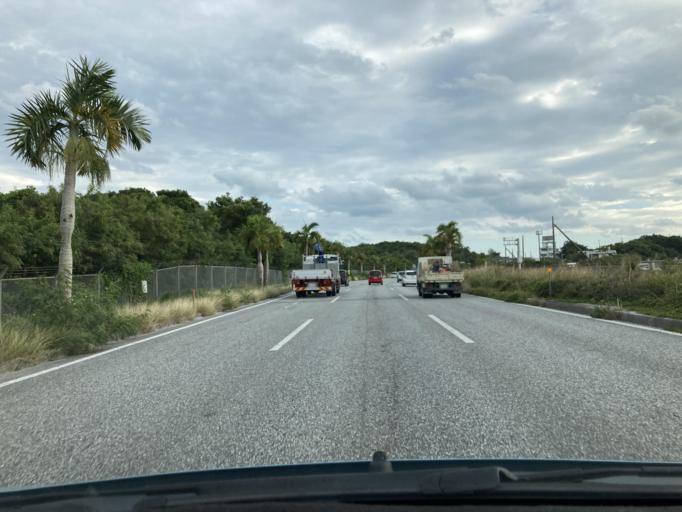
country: JP
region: Okinawa
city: Chatan
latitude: 26.3397
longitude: 127.7507
